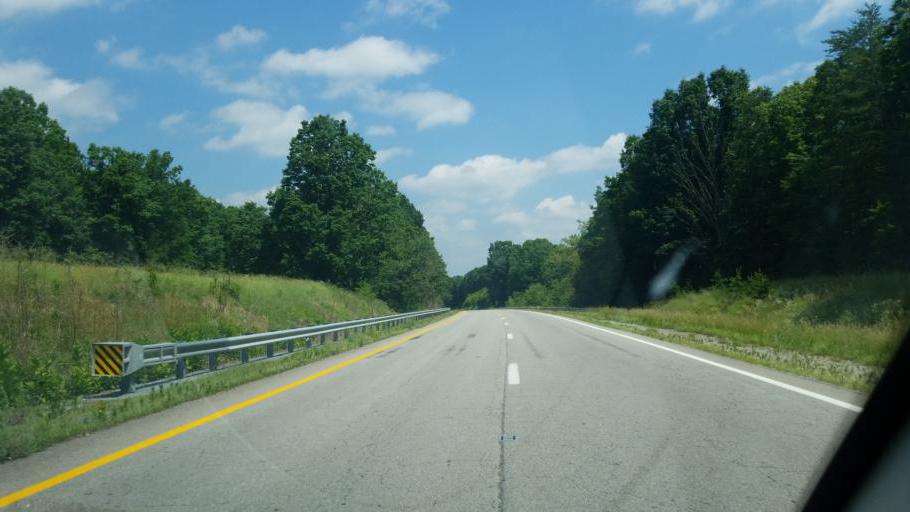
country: US
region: Virginia
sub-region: Pittsylvania County
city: Motley
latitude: 37.0855
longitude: -79.3322
